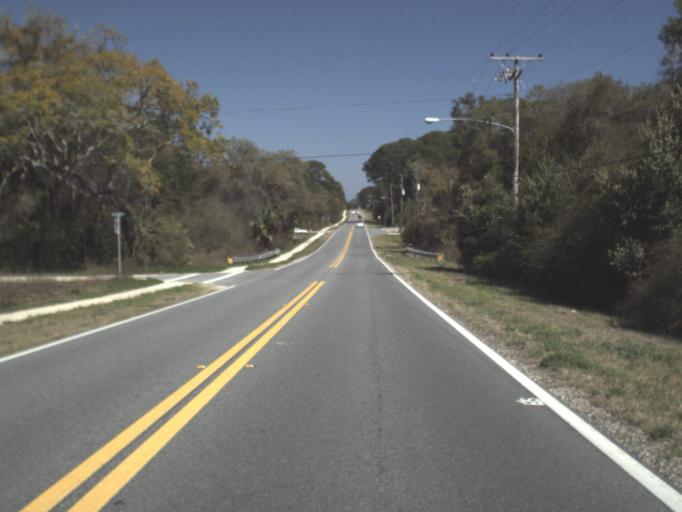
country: US
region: Florida
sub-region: Franklin County
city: Carrabelle
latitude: 29.8501
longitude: -84.6560
